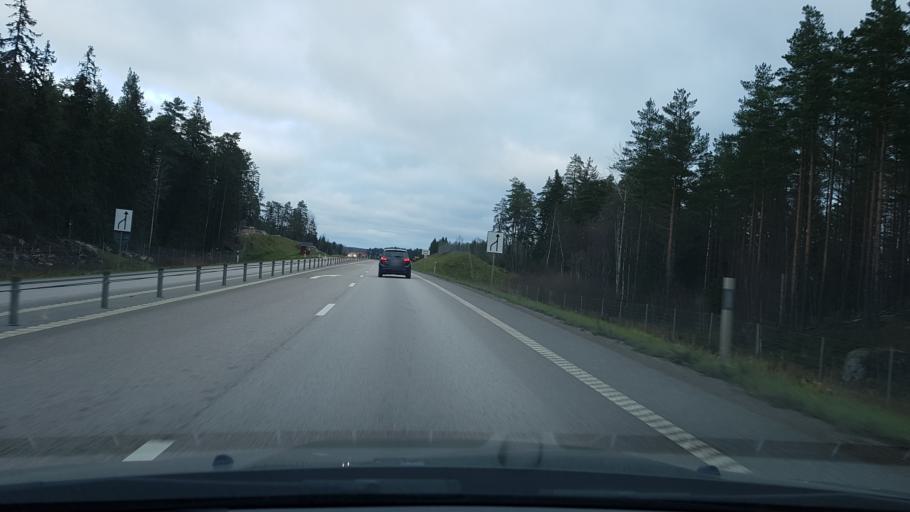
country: SE
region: Uppsala
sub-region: Uppsala Kommun
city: Storvreta
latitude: 59.9299
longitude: 17.7995
